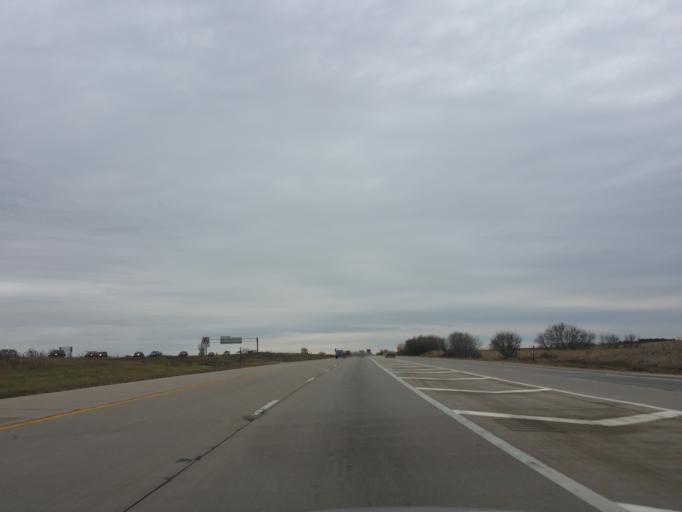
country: US
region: Wisconsin
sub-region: Columbia County
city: Portage
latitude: 43.4804
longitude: -89.4927
